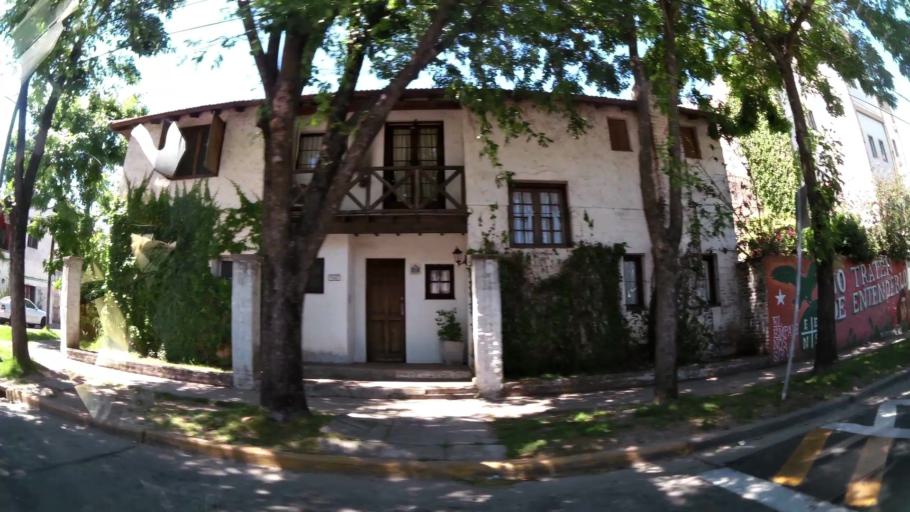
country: AR
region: Buenos Aires
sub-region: Partido de San Isidro
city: San Isidro
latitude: -34.4736
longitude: -58.5296
